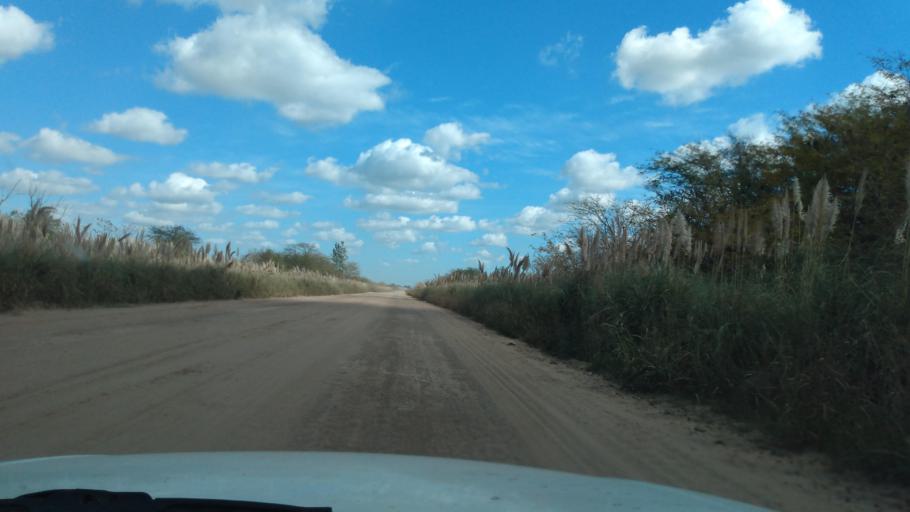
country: AR
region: Buenos Aires
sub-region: Partido de Navarro
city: Navarro
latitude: -35.0008
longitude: -59.3474
